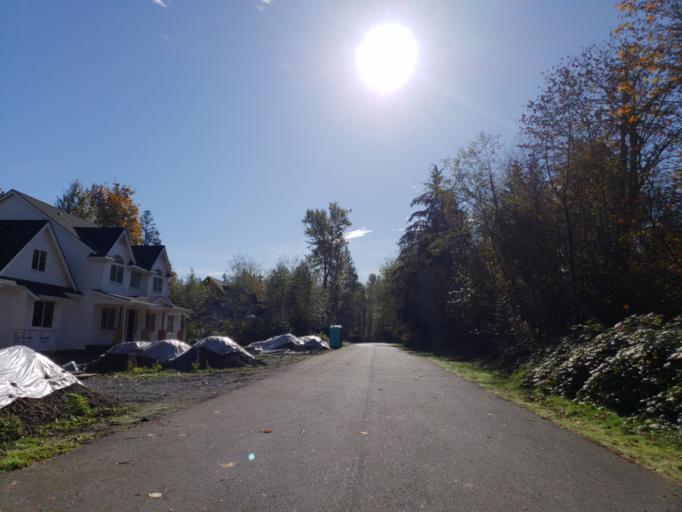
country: US
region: Washington
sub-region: King County
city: Lake Morton-Berrydale
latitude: 47.3058
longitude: -122.1365
